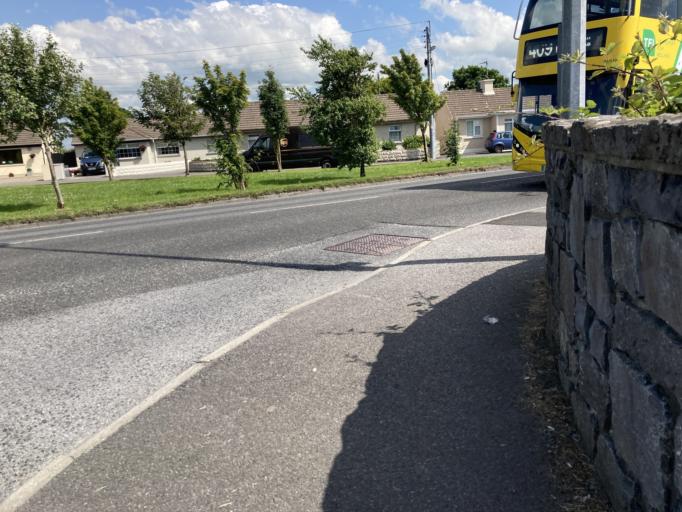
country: IE
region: Connaught
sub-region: County Galway
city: Claregalway
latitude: 53.2973
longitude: -8.9863
